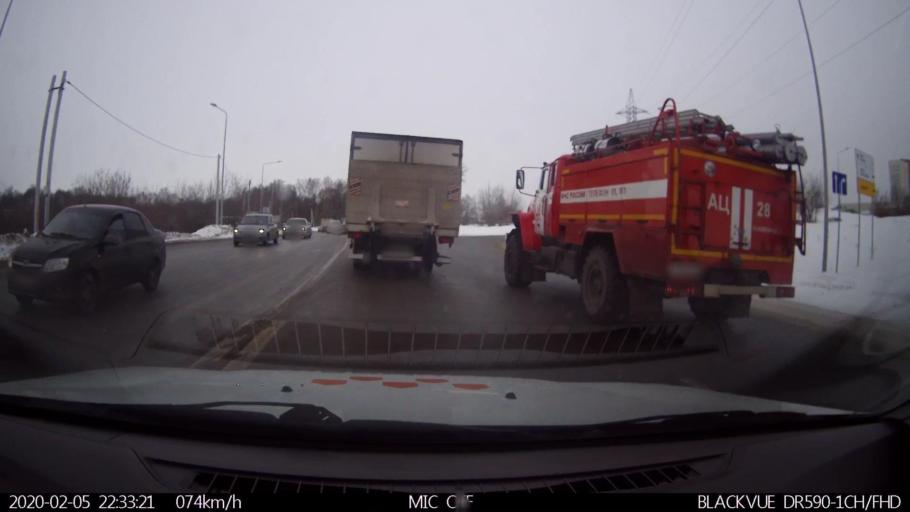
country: RU
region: Nizjnij Novgorod
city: Imeni Stepana Razina
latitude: 54.7365
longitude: 44.2081
